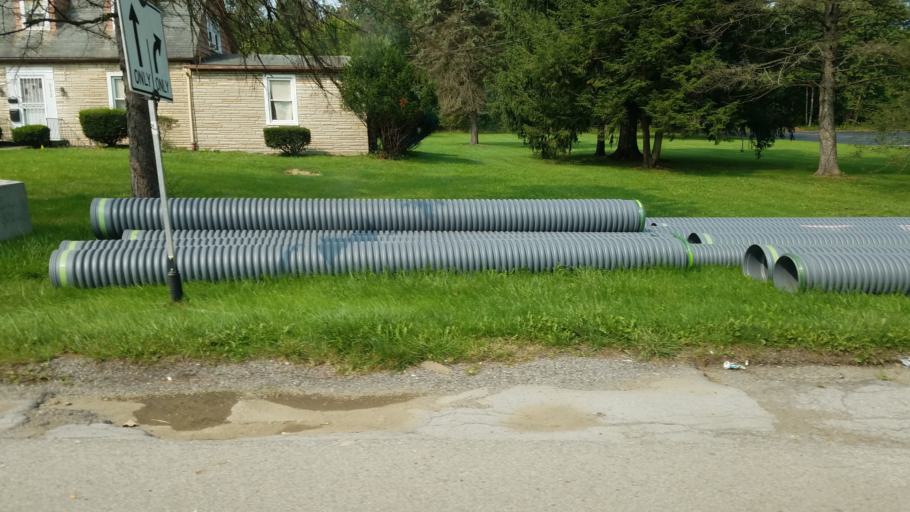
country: US
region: Ohio
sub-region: Mahoning County
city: Struthers
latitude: 41.0471
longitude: -80.6349
